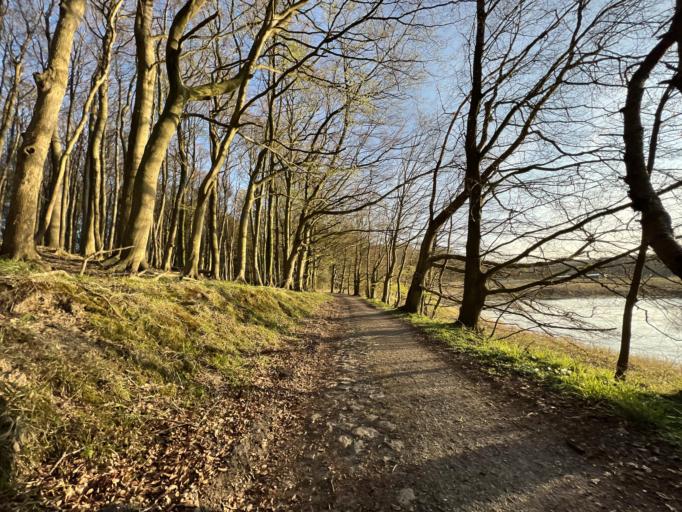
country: DE
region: Mecklenburg-Vorpommern
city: Sassnitz
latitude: 54.5336
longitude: 13.6532
